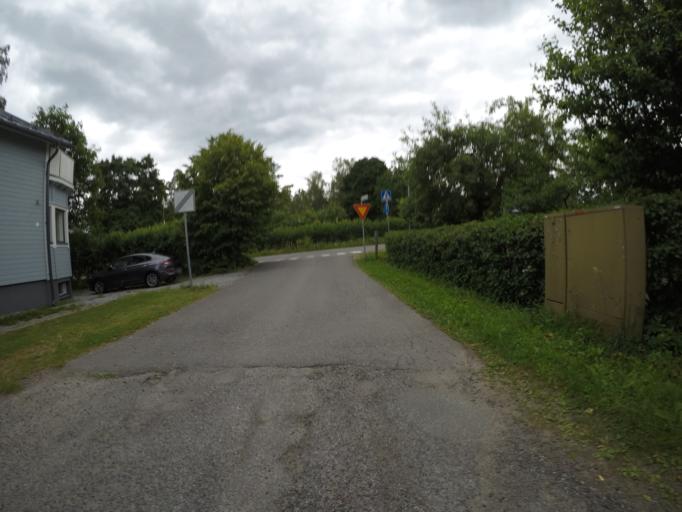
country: FI
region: Haeme
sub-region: Haemeenlinna
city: Haemeenlinna
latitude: 60.9805
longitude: 24.4504
